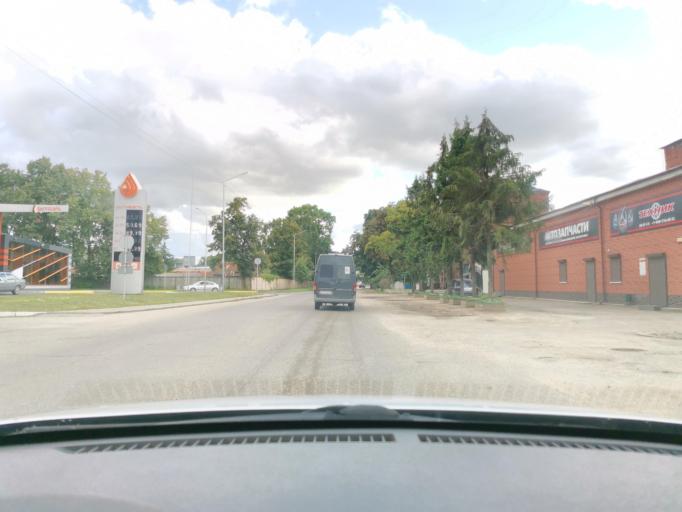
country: RU
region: Kaliningrad
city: Chernyakhovsk
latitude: 54.6457
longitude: 21.8090
